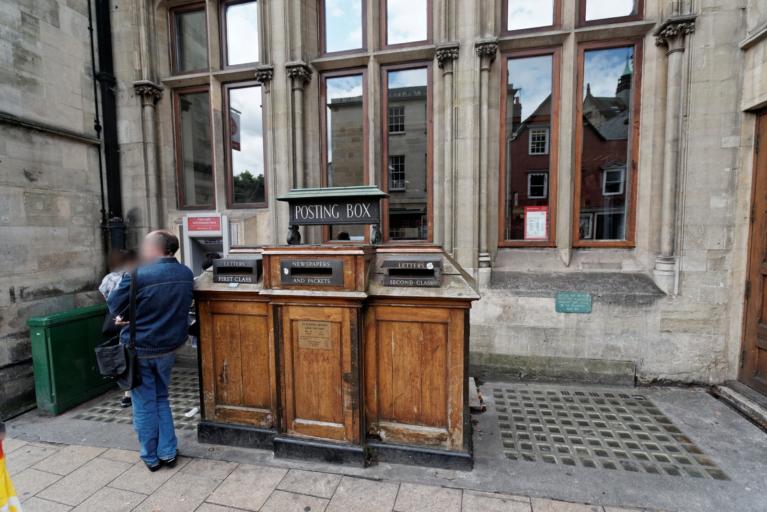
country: GB
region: England
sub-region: Oxfordshire
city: Oxford
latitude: 51.7511
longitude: -1.2571
